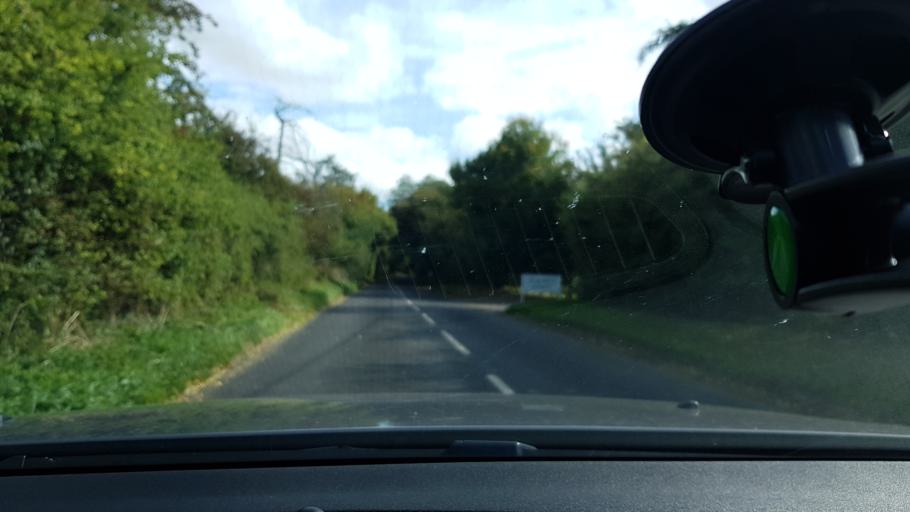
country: GB
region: England
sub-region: West Berkshire
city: Lambourn
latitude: 51.5167
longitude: -1.5431
